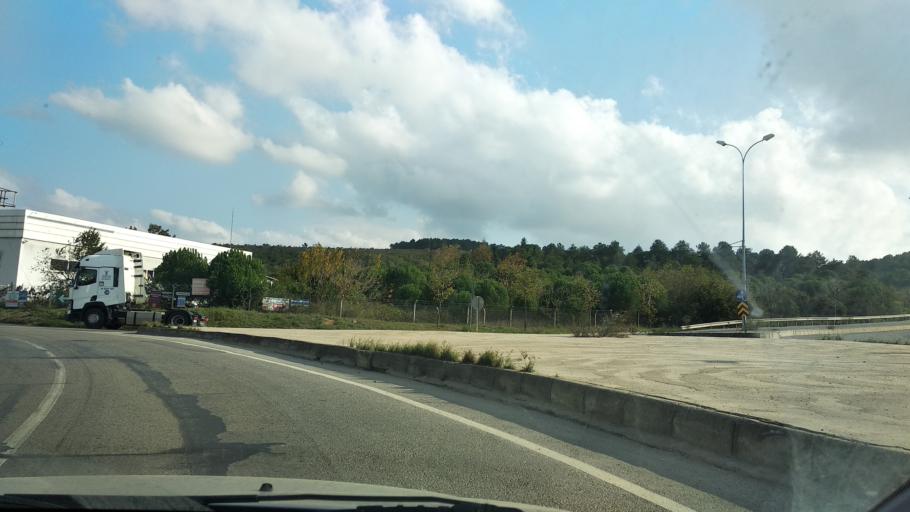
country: TR
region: Istanbul
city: Sultanbeyli
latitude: 40.9305
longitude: 29.3348
